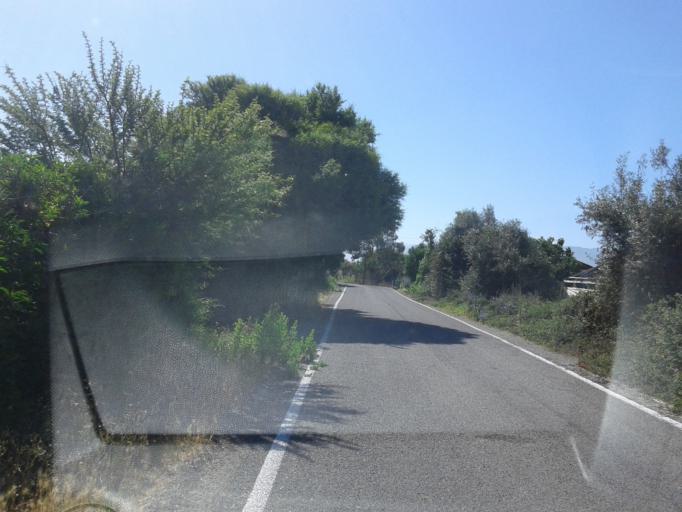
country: CL
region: Valparaiso
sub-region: Provincia de Marga Marga
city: Limache
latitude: -32.9793
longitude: -71.2971
